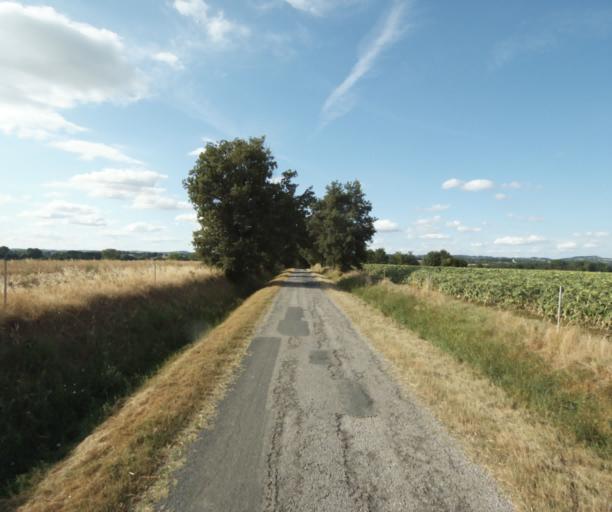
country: FR
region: Midi-Pyrenees
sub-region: Departement de la Haute-Garonne
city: Revel
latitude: 43.5089
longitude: 1.9970
